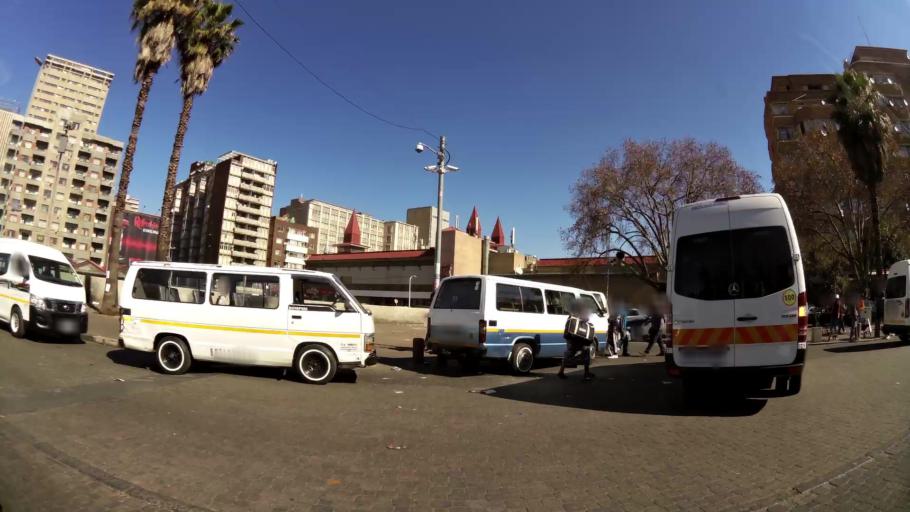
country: ZA
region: Gauteng
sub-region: City of Johannesburg Metropolitan Municipality
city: Johannesburg
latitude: -26.1972
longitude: 28.0462
